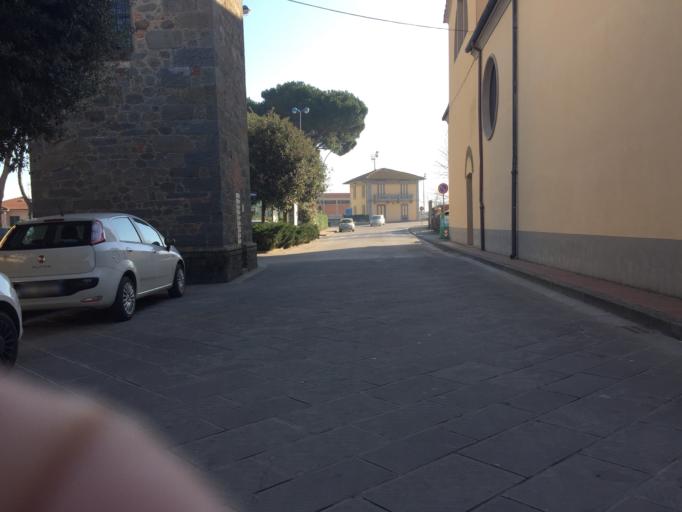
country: IT
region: Tuscany
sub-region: Provincia di Pistoia
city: Ponte Buggianese
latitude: 43.8411
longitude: 10.7479
